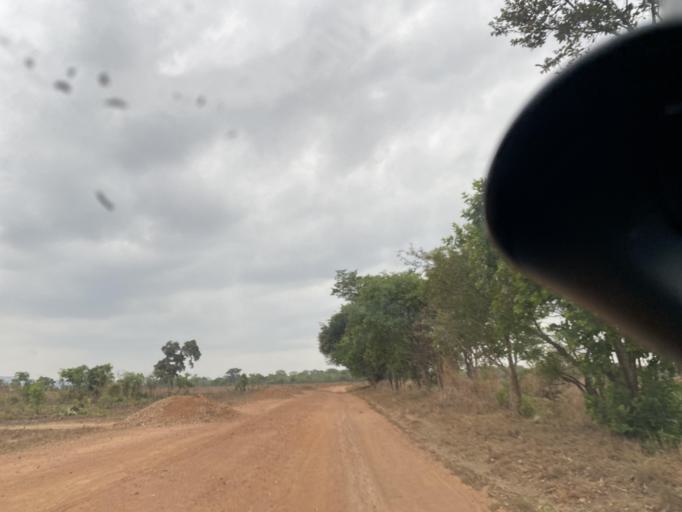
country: ZM
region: Lusaka
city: Chongwe
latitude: -15.2273
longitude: 28.7299
